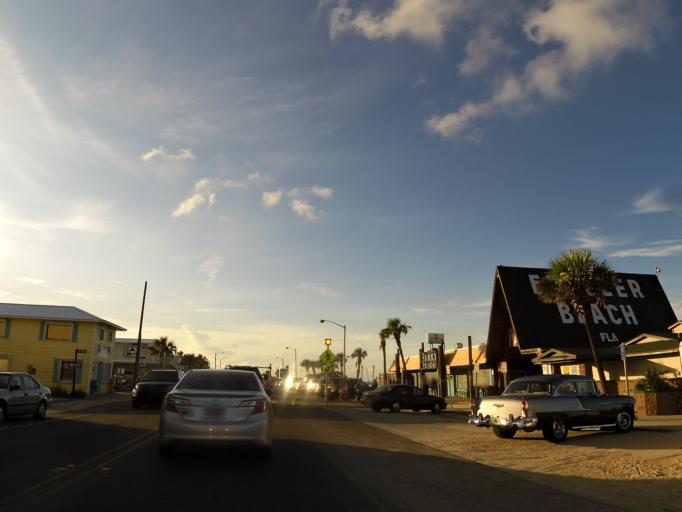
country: US
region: Florida
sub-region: Flagler County
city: Flagler Beach
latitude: 29.4795
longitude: -81.1267
